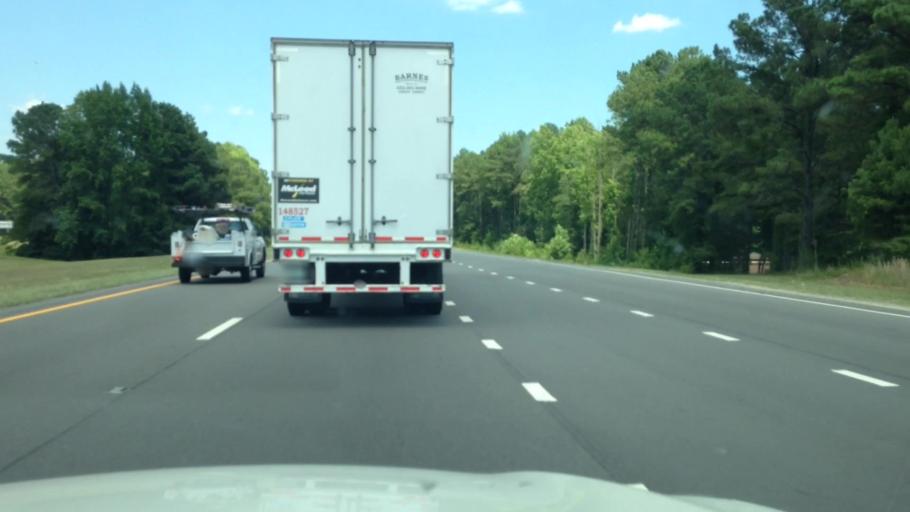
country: US
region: North Carolina
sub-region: Cumberland County
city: Hope Mills
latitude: 34.9398
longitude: -78.9179
